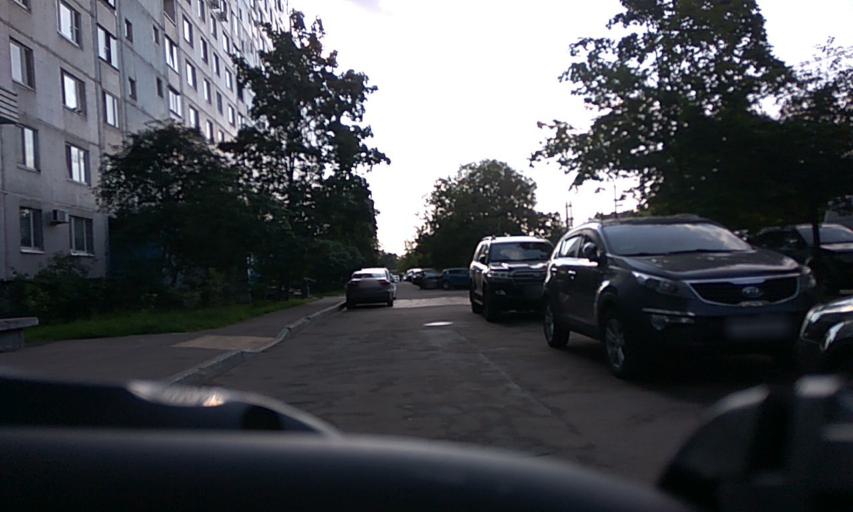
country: RU
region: Moscow
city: Kolomenskoye
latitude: 55.6794
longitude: 37.6995
